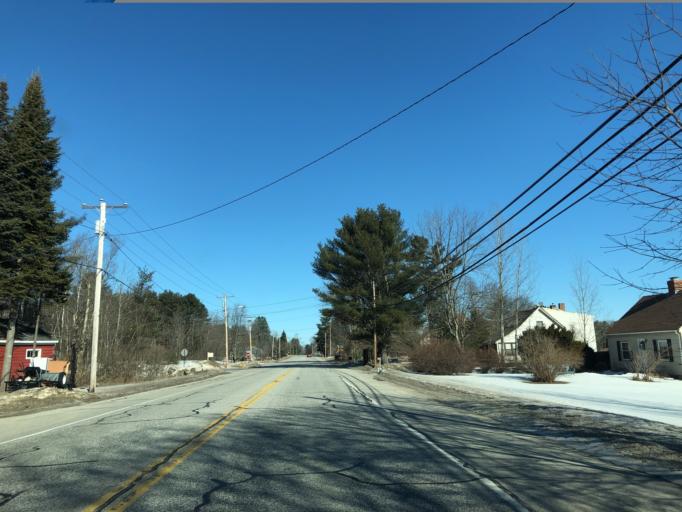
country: US
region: Maine
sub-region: Cumberland County
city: North Windham
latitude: 43.7927
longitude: -70.4079
